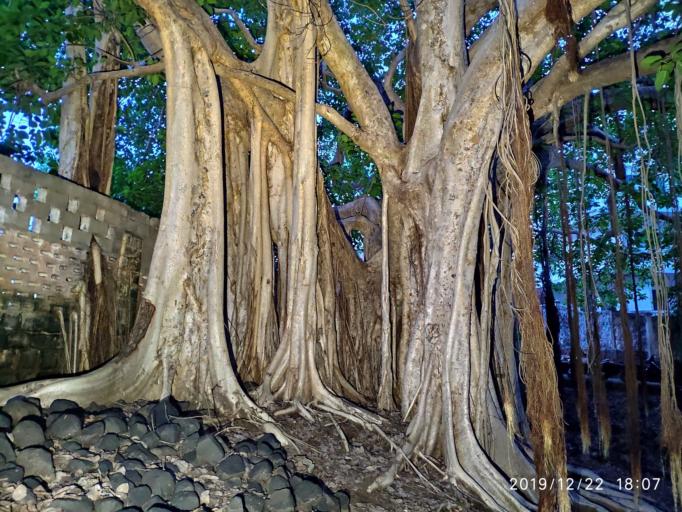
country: MG
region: Diana
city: Antsiranana
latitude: -12.2689
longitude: 49.2961
